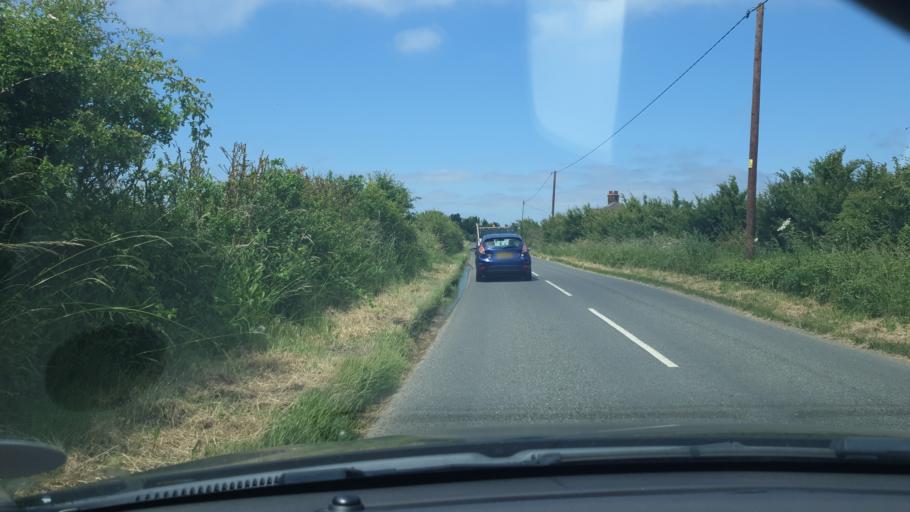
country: GB
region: England
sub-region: Essex
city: Clacton-on-Sea
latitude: 51.8189
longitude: 1.1854
